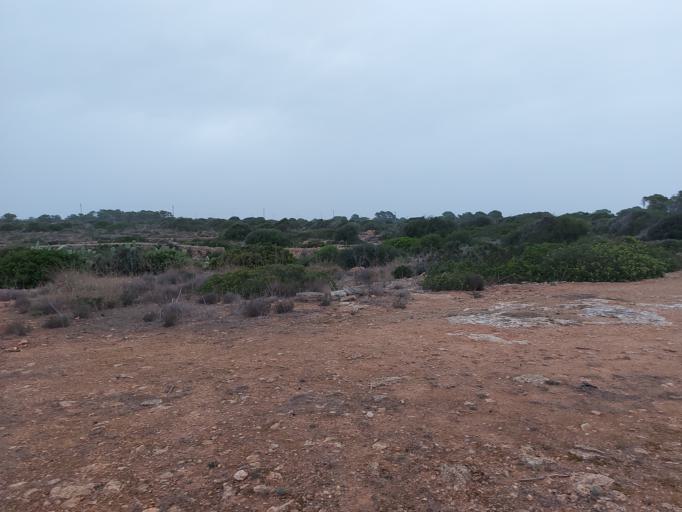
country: ES
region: Balearic Islands
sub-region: Illes Balears
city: s'Arenal
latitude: 39.3630
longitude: 2.7907
